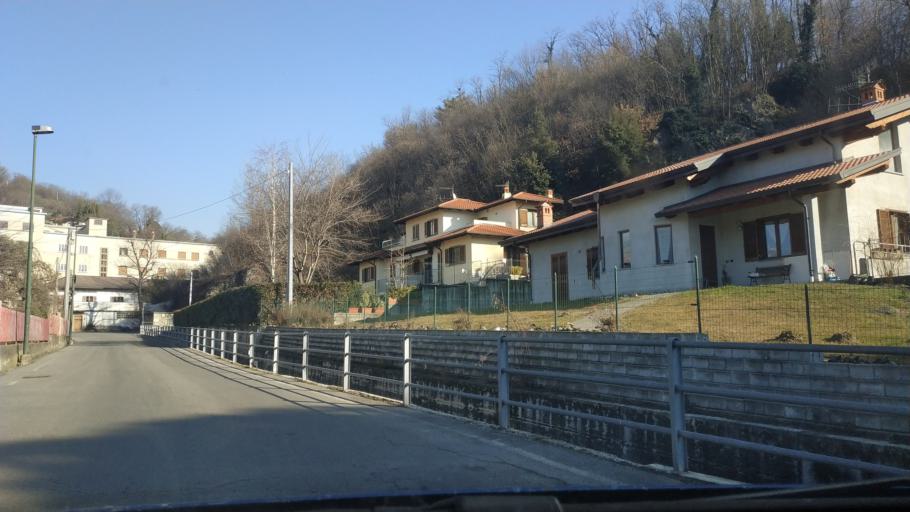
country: IT
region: Piedmont
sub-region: Provincia di Torino
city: Montalto Dora
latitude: 45.4896
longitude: 7.8665
